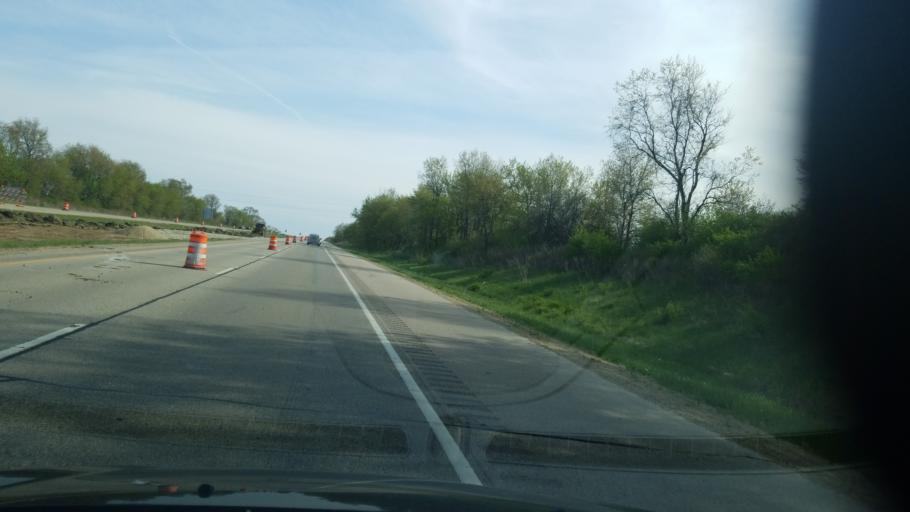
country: US
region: Wisconsin
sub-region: Dane County
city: Oregon
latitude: 42.9936
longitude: -89.3863
